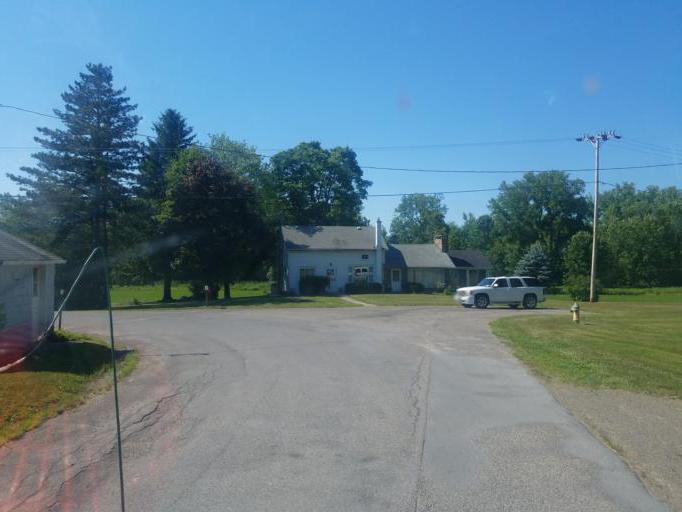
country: US
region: New York
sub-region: Wayne County
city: Newark
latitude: 43.0603
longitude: -77.0456
